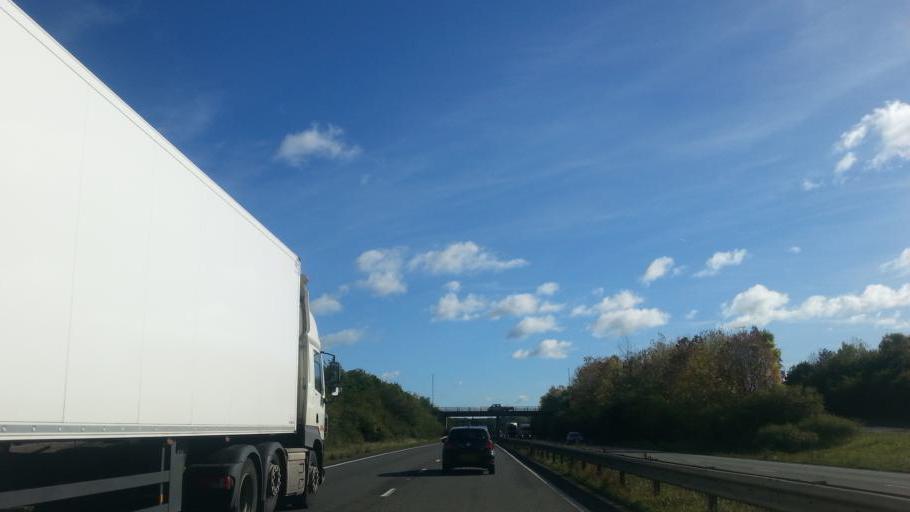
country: GB
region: England
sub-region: Northamptonshire
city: Thrapston
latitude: 52.3908
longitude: -0.5599
